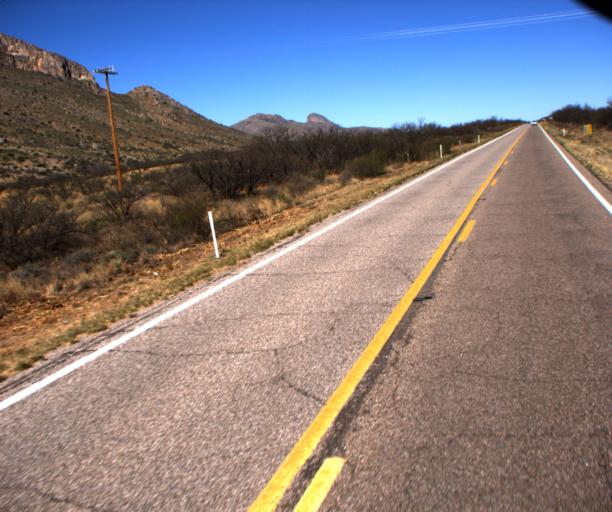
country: US
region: Arizona
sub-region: Cochise County
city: Huachuca City
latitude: 31.6966
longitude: -110.4218
